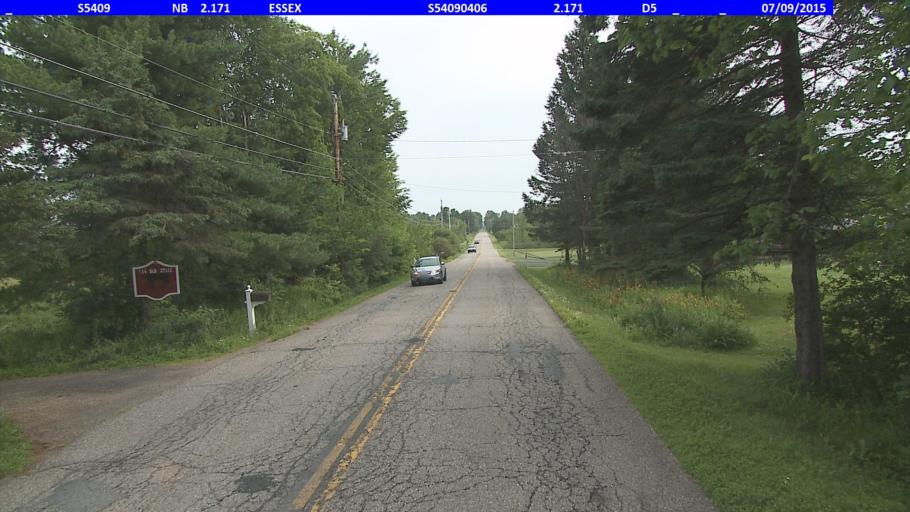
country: US
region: Vermont
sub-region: Chittenden County
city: Essex Junction
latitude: 44.5401
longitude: -73.0734
